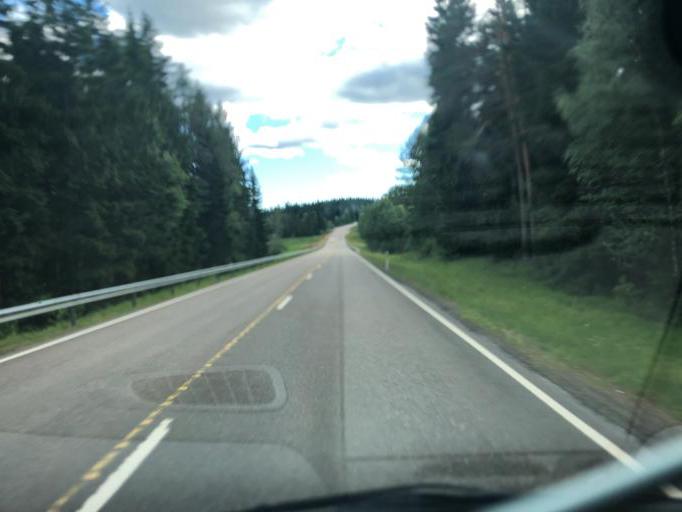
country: FI
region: Southern Savonia
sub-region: Mikkeli
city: Maentyharju
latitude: 61.0665
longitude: 27.0543
